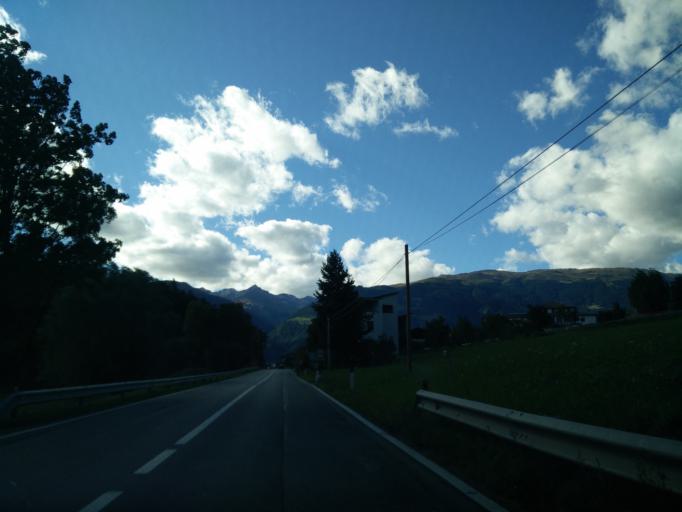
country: IT
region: Trentino-Alto Adige
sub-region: Bolzano
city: Glorenza
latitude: 46.6799
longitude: 10.5657
